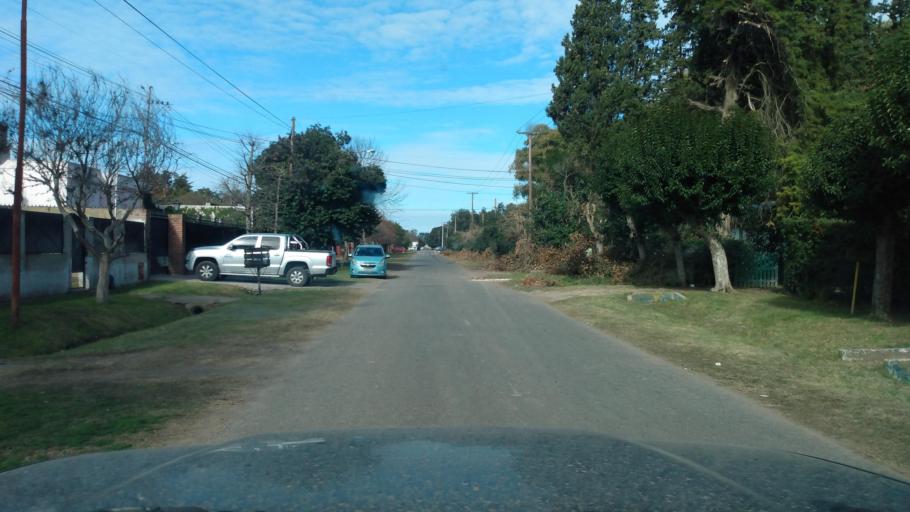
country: AR
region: Buenos Aires
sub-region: Partido de Lujan
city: Lujan
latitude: -34.5973
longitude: -59.1823
